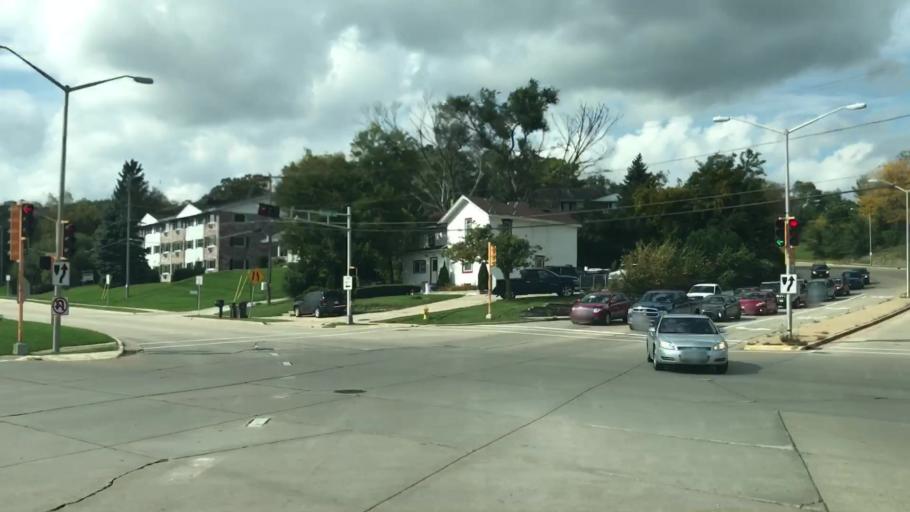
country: US
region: Wisconsin
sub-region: Waukesha County
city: Waukesha
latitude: 43.0227
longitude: -88.2225
